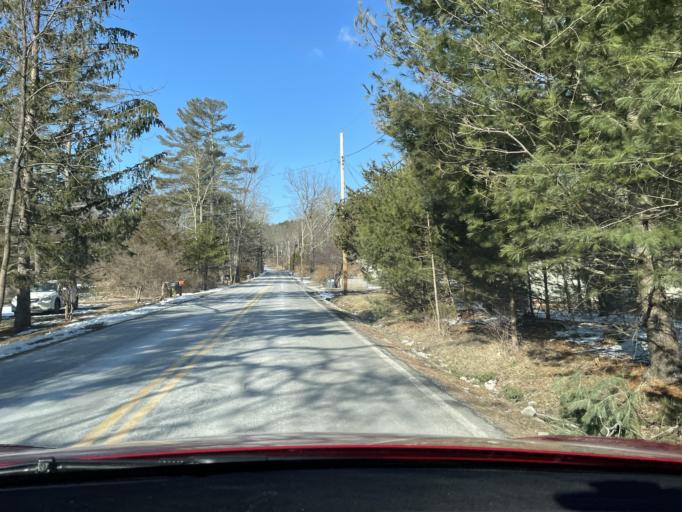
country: US
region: New York
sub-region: Ulster County
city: Woodstock
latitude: 42.0496
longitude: -74.1207
